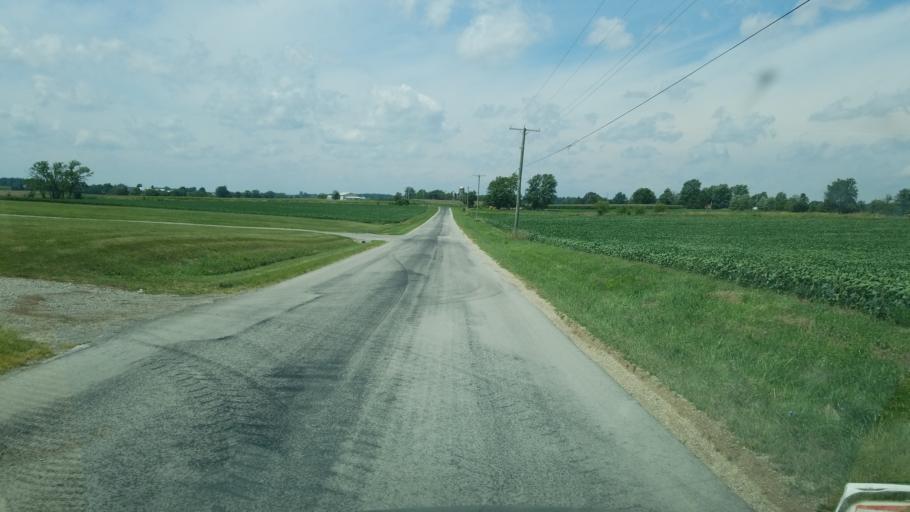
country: US
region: Ohio
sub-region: Hardin County
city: Forest
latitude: 40.8654
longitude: -83.4819
